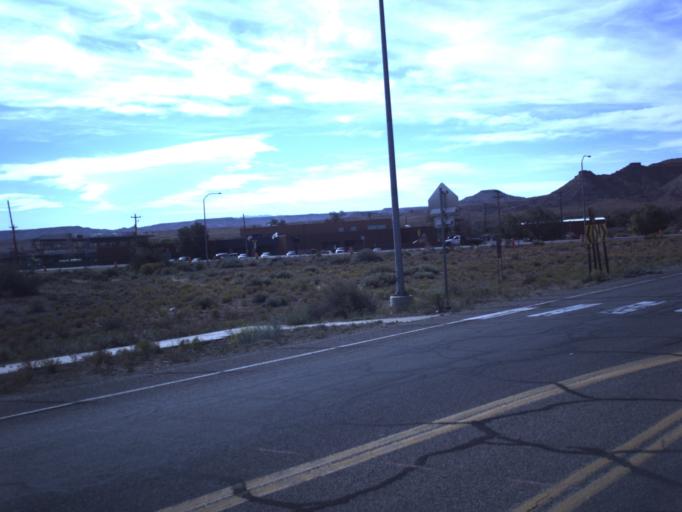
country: US
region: Utah
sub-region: San Juan County
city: Blanding
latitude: 37.2627
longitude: -109.3057
